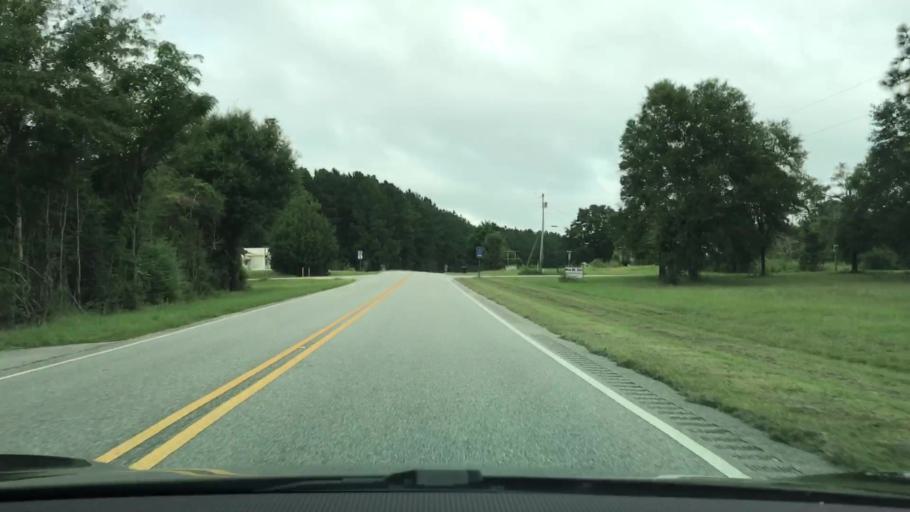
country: US
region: Alabama
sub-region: Geneva County
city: Samson
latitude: 31.0173
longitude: -86.1252
